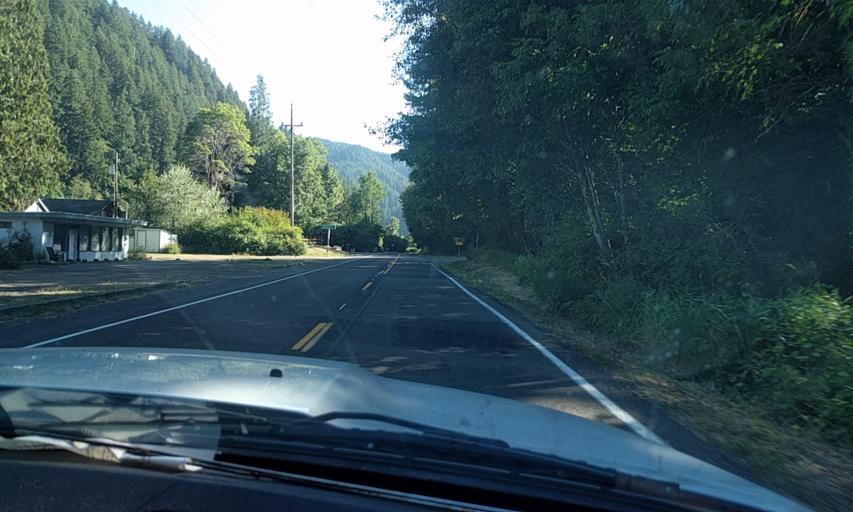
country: US
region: Oregon
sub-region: Lane County
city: Florence
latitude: 44.0673
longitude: -123.8802
